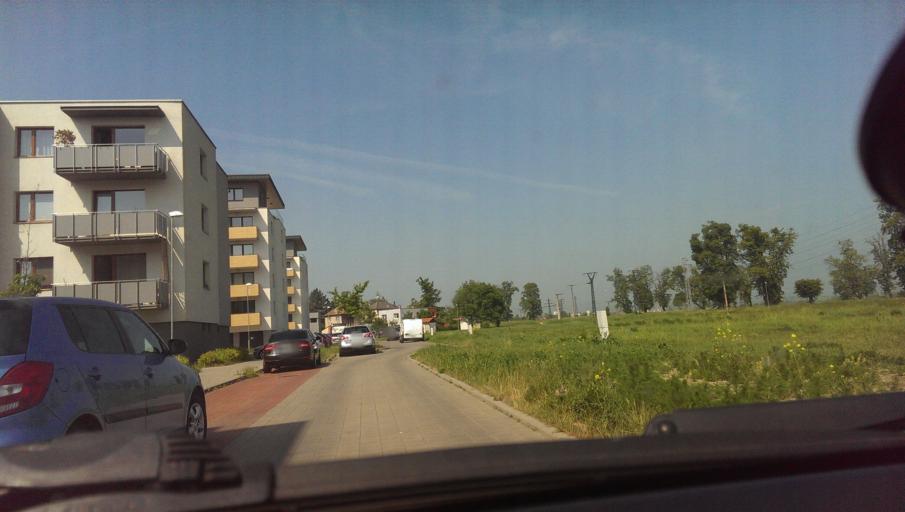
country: CZ
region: Zlin
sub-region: Okres Uherske Hradiste
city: Uherske Hradiste
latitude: 49.0725
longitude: 17.4729
